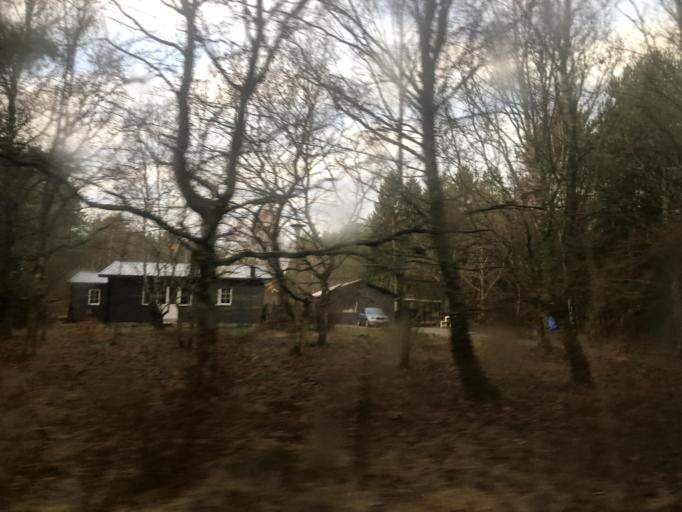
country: SE
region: Skane
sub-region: Sjobo Kommun
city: Blentarp
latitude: 55.6158
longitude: 13.5474
